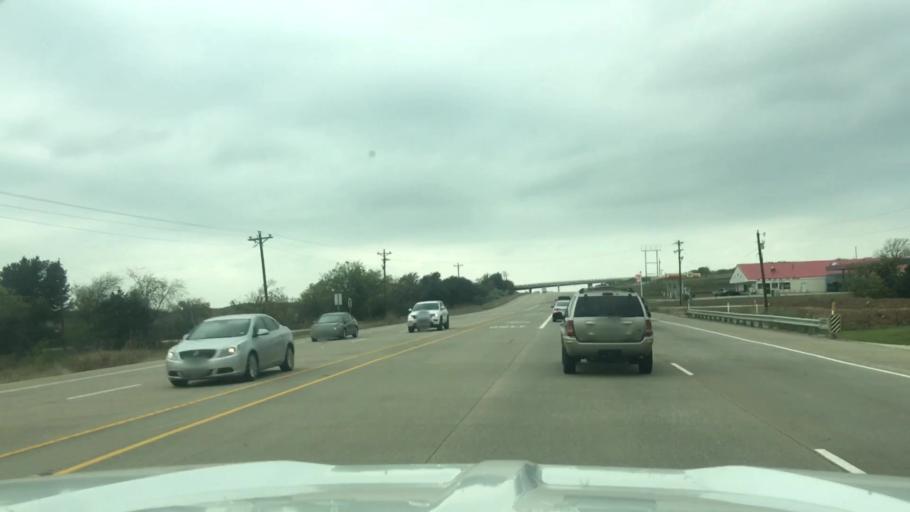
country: US
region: Texas
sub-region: Denton County
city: Cross Roads
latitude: 33.2298
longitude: -97.0001
